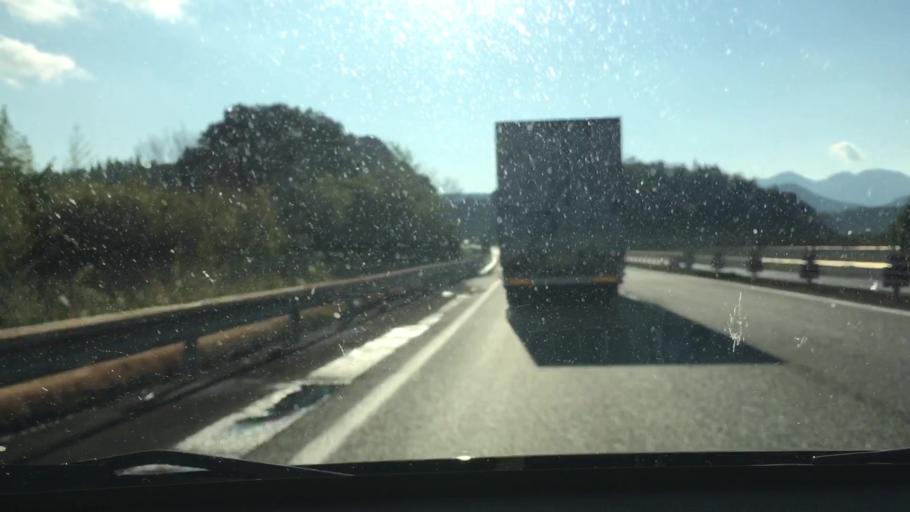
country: JP
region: Kagoshima
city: Okuchi-shinohara
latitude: 31.9403
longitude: 130.7125
